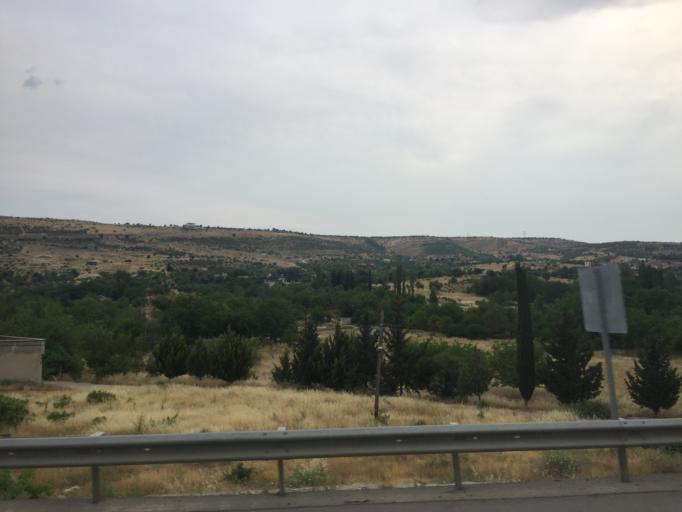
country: TR
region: Gaziantep
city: Gaziantep
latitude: 37.0053
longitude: 37.4330
